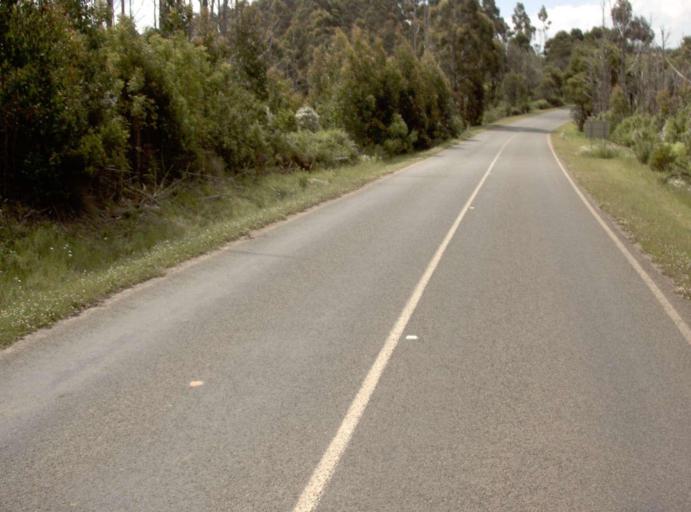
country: AU
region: Victoria
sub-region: Latrobe
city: Traralgon
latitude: -38.4144
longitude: 146.5661
